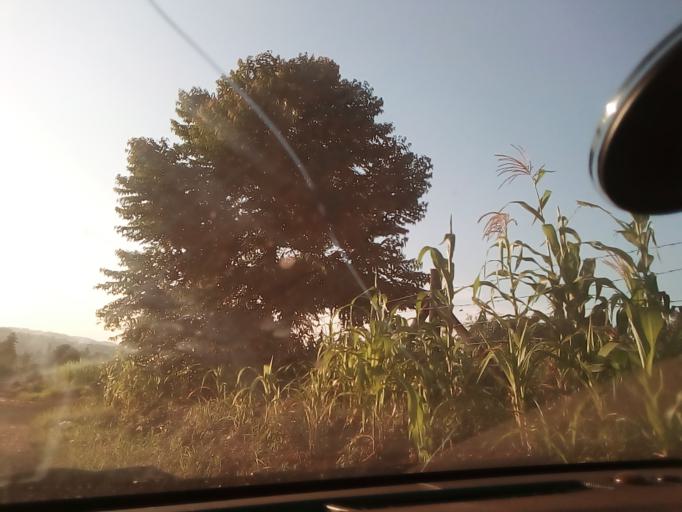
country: UG
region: Central Region
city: Masaka
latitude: -0.3360
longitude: 31.7577
